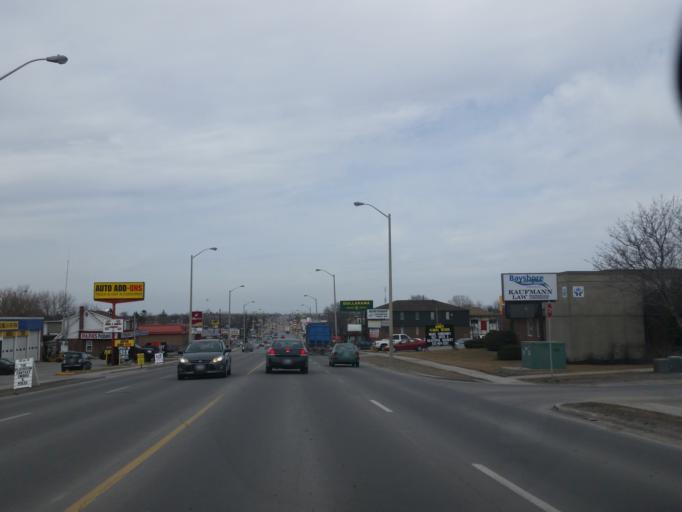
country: CA
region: Ontario
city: Belleville
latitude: 44.1790
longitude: -77.3918
